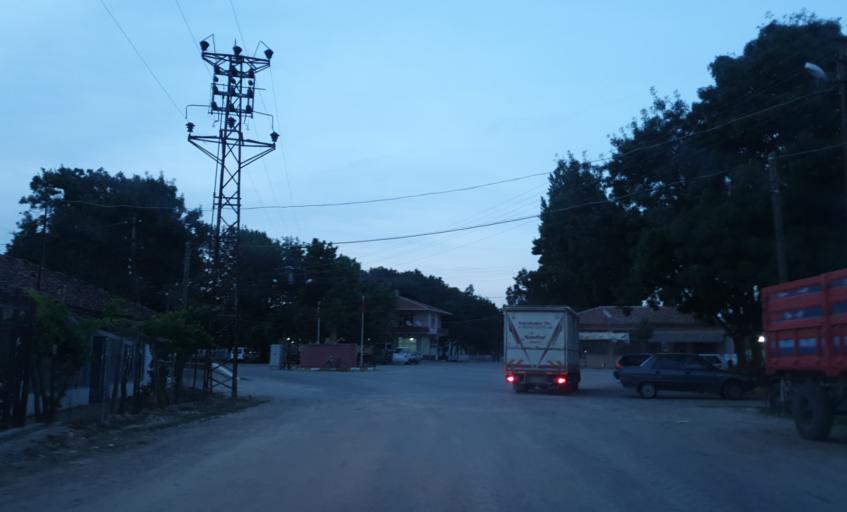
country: TR
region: Kirklareli
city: Vize
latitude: 41.4873
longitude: 27.7530
